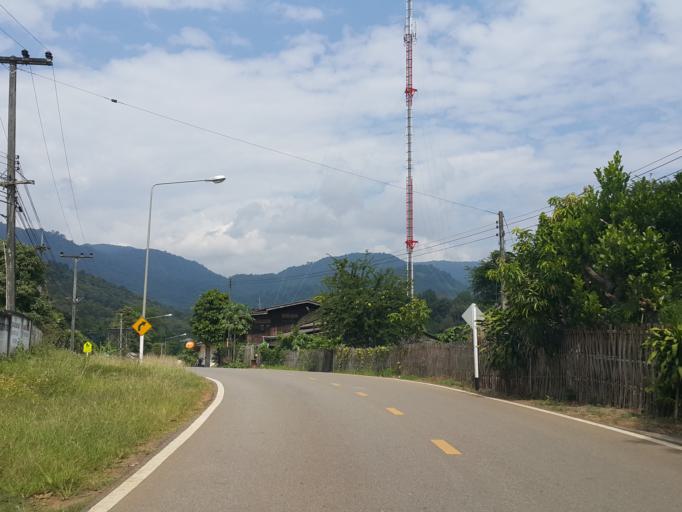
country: TH
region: Mae Hong Son
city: Mae Hong Son
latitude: 19.4654
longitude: 97.9681
